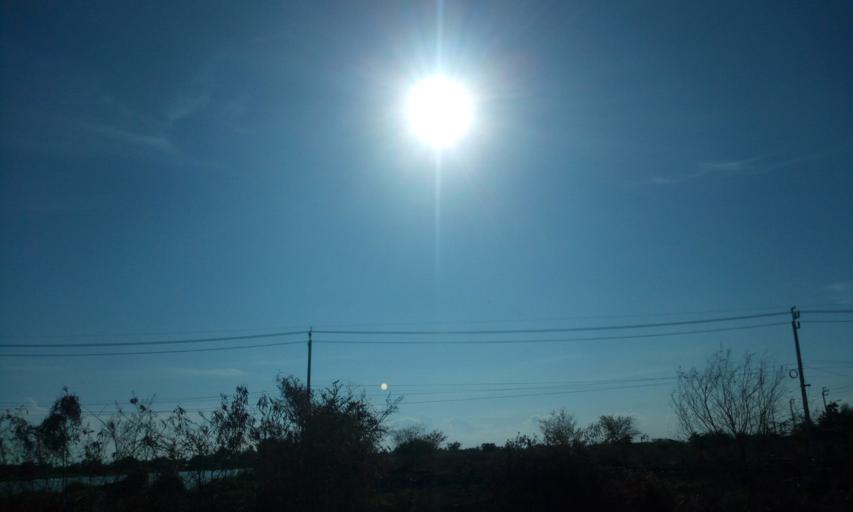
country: TH
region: Samut Prakan
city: Bang Bo District
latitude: 13.5357
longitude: 100.7496
